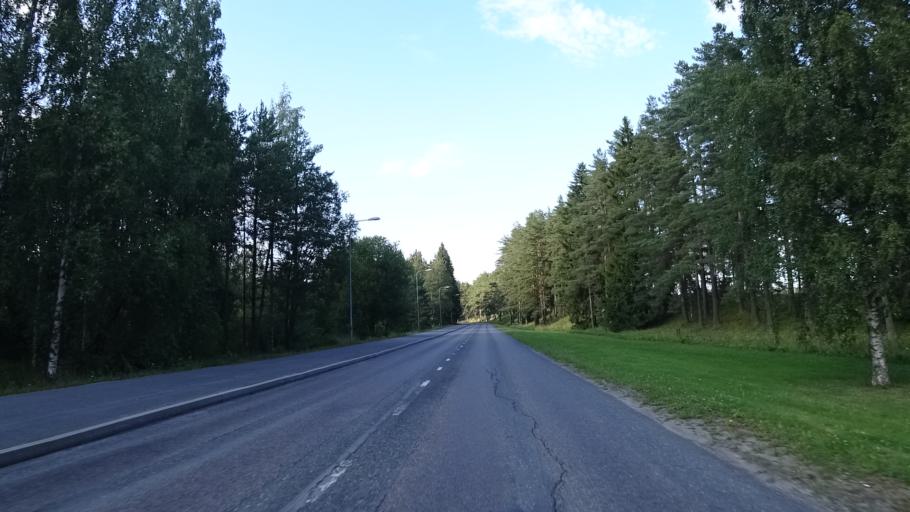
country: FI
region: South Karelia
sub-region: Imatra
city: Imatra
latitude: 61.1773
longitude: 28.7796
